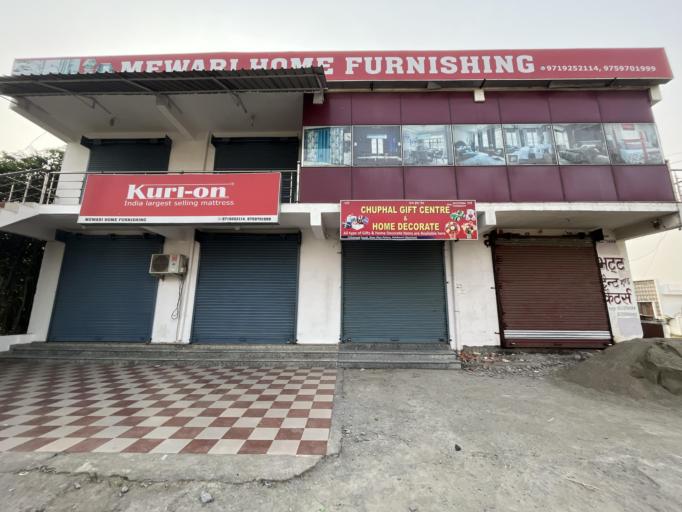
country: IN
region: Uttarakhand
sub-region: Naini Tal
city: Haldwani
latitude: 29.1989
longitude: 79.4864
